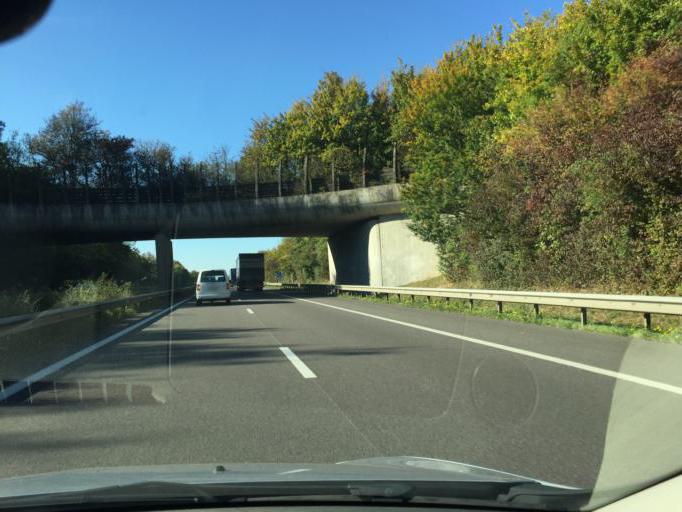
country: LU
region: Grevenmacher
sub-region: Canton de Grevenmacher
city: Flaxweiler
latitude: 49.6513
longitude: 6.3341
